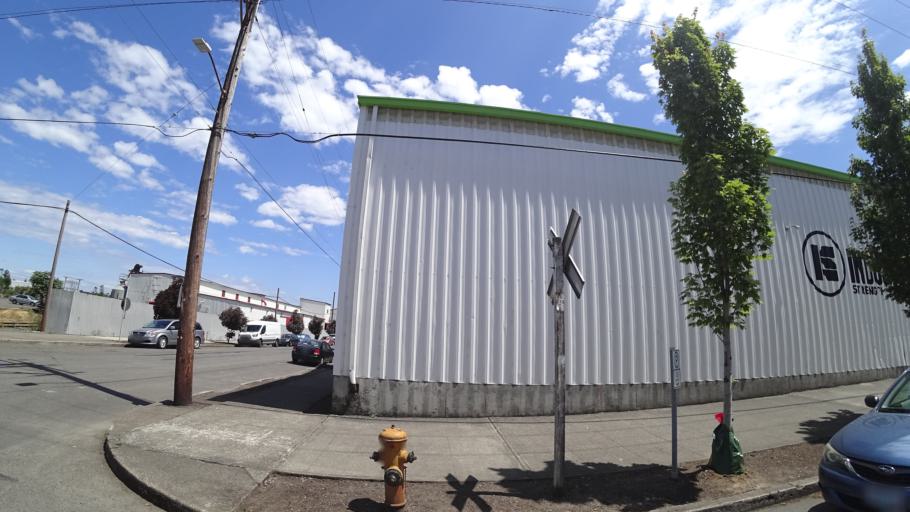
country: US
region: Oregon
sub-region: Multnomah County
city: Portland
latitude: 45.5374
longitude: -122.7049
